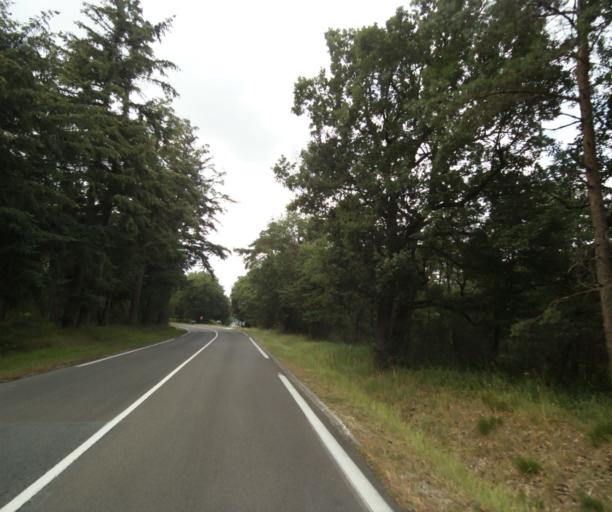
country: FR
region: Ile-de-France
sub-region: Departement de Seine-et-Marne
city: Barbizon
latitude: 48.4170
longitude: 2.6219
